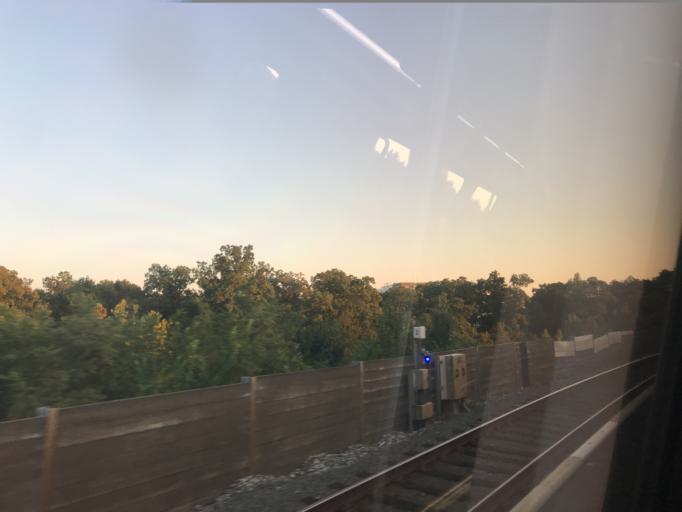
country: US
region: Maryland
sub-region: Prince George's County
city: College Park
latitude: 38.9736
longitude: -76.9302
